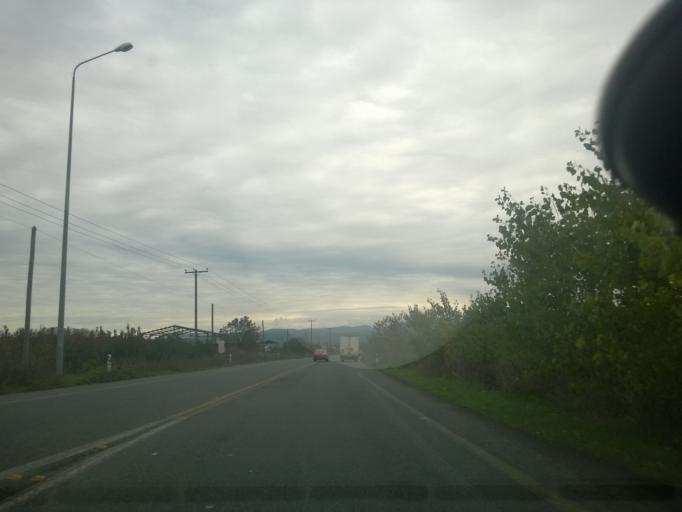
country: GR
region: Central Macedonia
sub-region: Nomos Pellis
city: Apsalos
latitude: 40.9264
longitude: 22.0832
